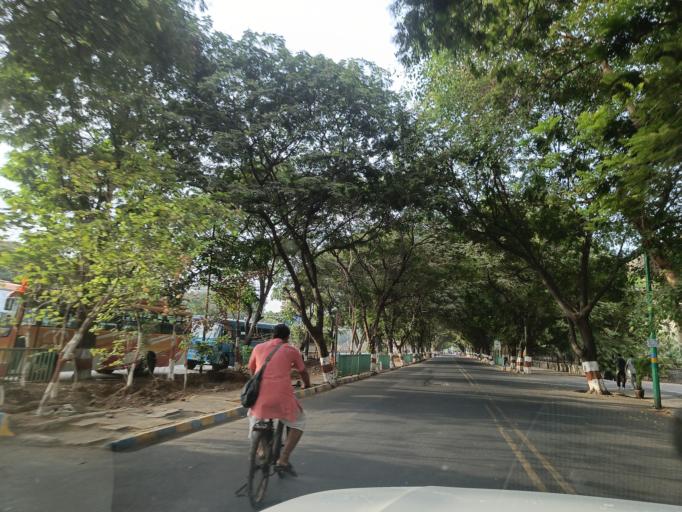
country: IN
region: Maharashtra
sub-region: Thane
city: Thane
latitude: 19.1863
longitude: 72.9640
